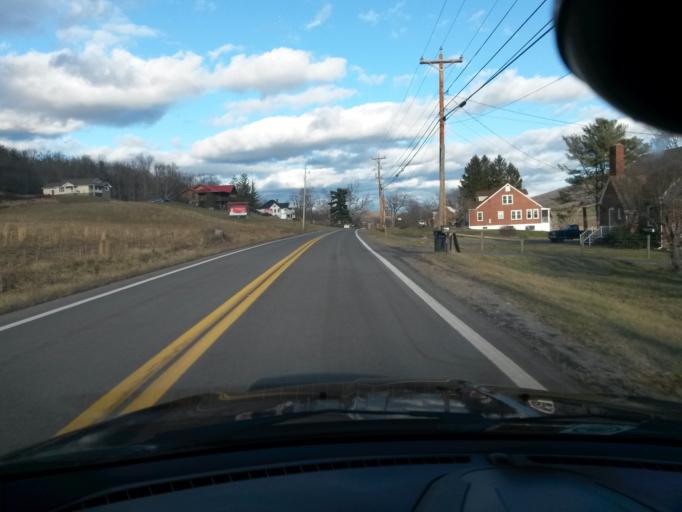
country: US
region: Virginia
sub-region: Giles County
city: Pearisburg
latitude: 37.4121
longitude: -80.7520
